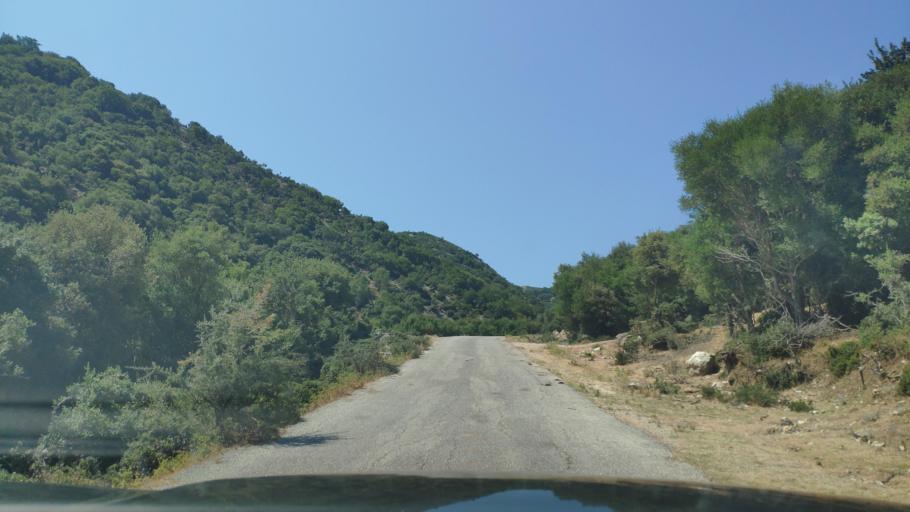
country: GR
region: West Greece
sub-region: Nomos Aitolias kai Akarnanias
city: Monastirakion
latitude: 38.8326
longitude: 20.9325
